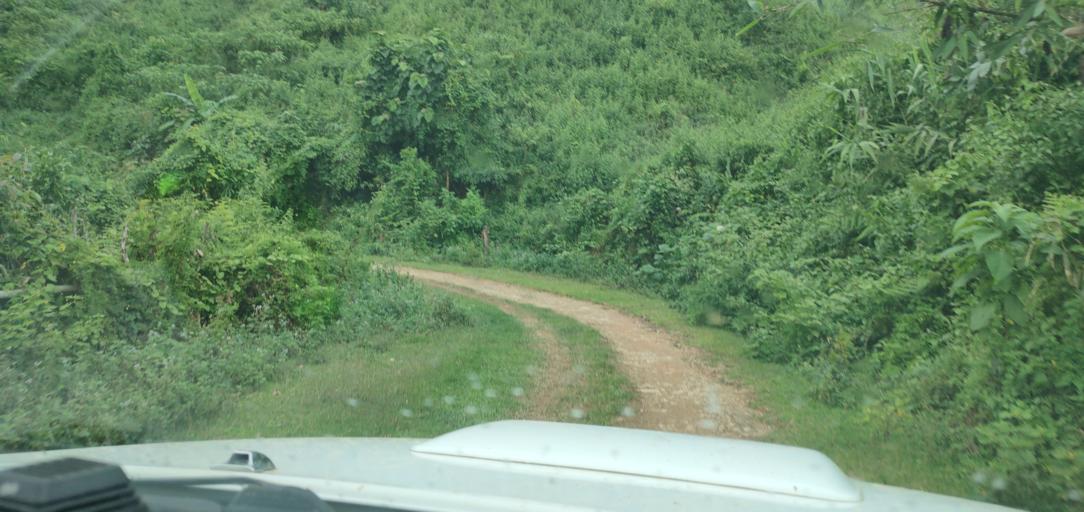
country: LA
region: Phongsali
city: Phongsali
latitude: 21.4400
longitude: 102.3307
